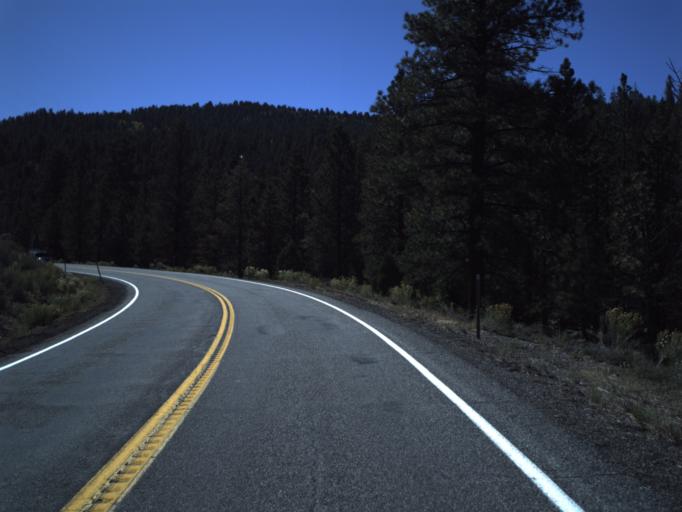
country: US
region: Utah
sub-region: Wayne County
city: Loa
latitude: 38.1780
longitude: -111.3469
